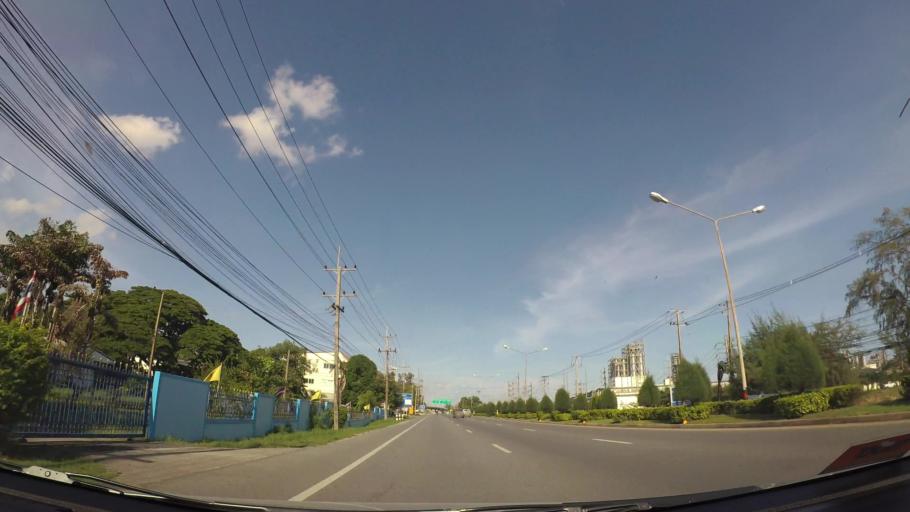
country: TH
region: Rayong
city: Rayong
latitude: 12.6638
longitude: 101.3050
